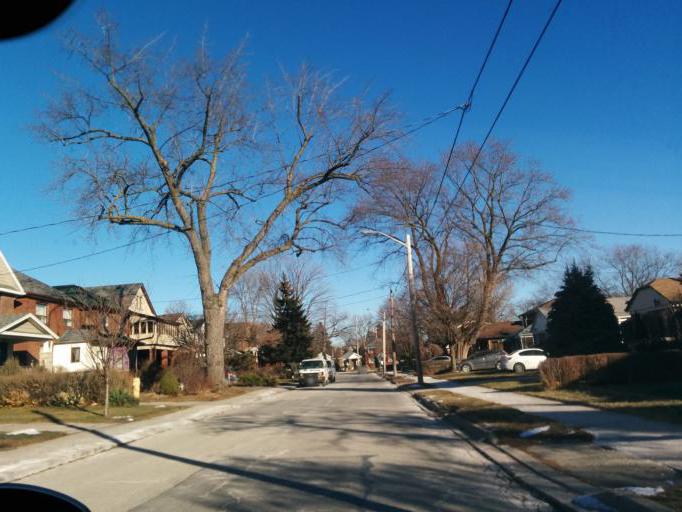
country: CA
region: Ontario
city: Etobicoke
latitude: 43.6055
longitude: -79.4960
